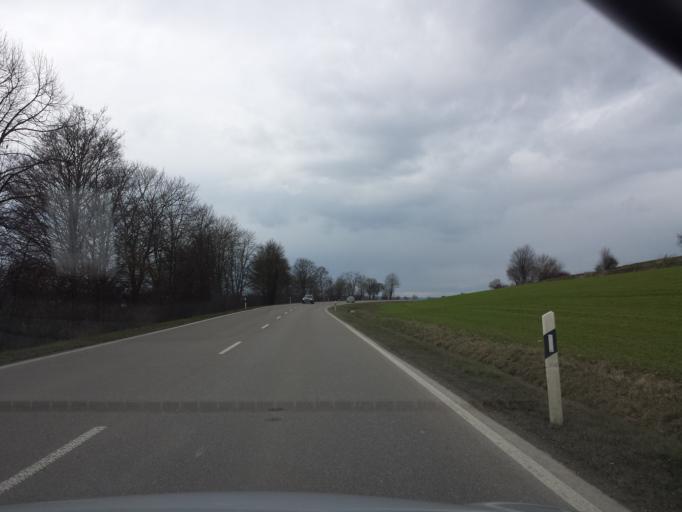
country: DE
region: Baden-Wuerttemberg
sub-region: Tuebingen Region
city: Burgrieden
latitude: 48.2452
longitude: 9.9232
